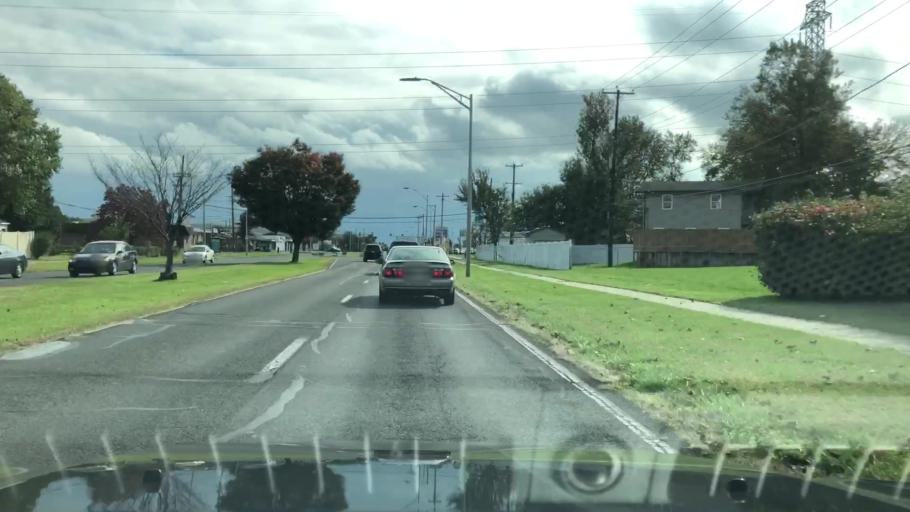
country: US
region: Pennsylvania
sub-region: Bucks County
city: Tullytown
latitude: 40.1463
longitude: -74.8221
